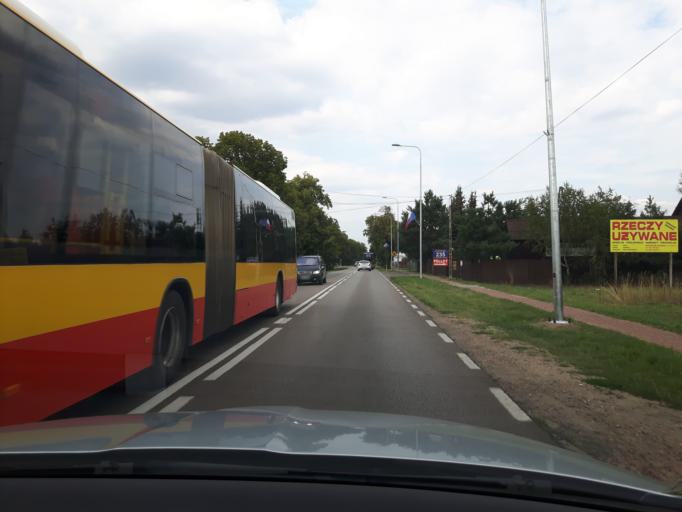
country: PL
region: Masovian Voivodeship
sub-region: Powiat legionowski
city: Nieporet
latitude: 52.4058
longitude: 21.0385
